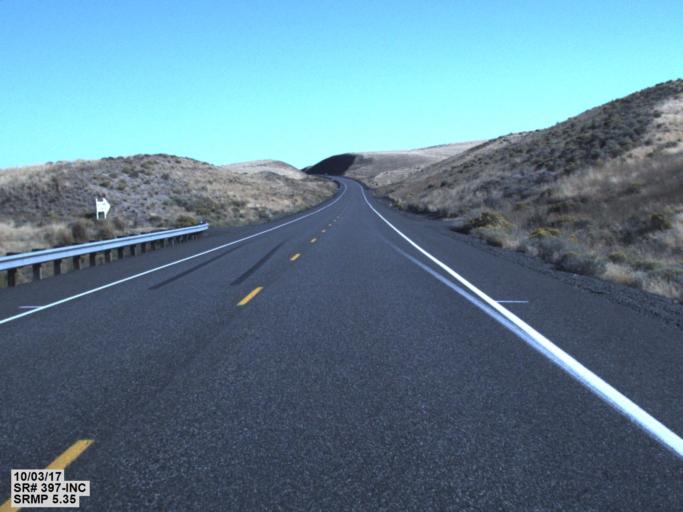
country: US
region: Washington
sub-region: Benton County
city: Highland
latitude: 46.1388
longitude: -119.1018
